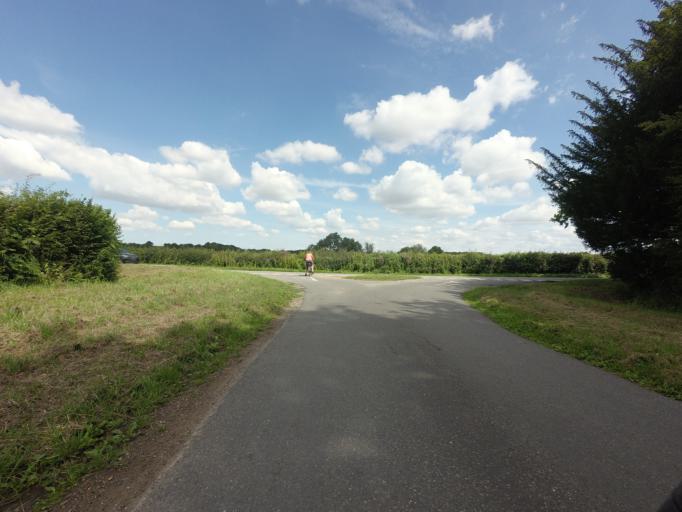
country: GB
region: England
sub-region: Kent
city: Tenterden
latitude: 51.0735
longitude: 0.7241
